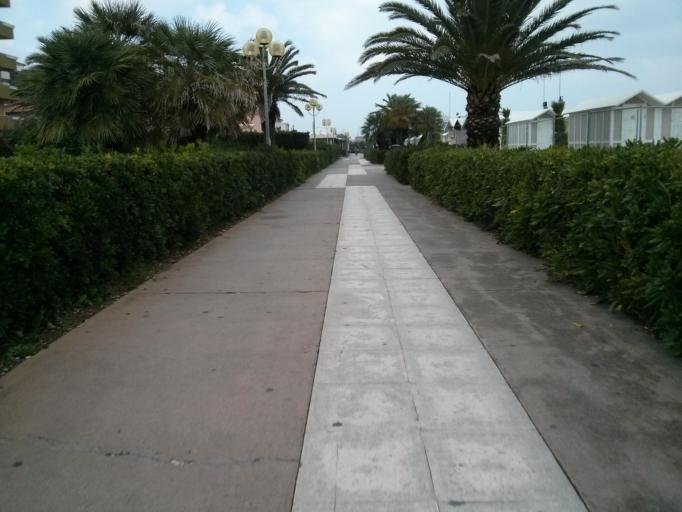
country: IT
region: The Marches
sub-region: Provincia di Pesaro e Urbino
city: Fano
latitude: 43.8475
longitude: 13.0235
